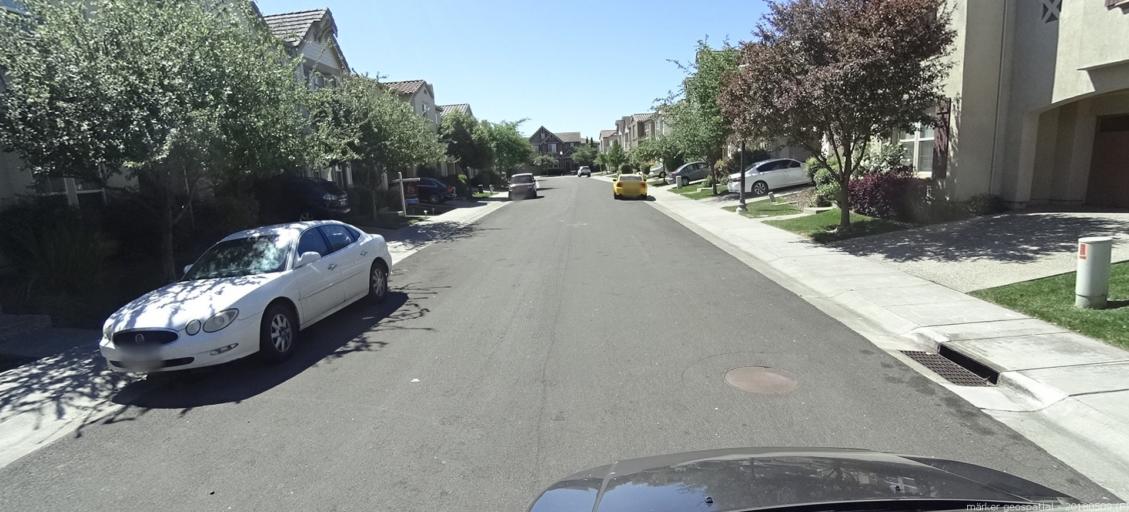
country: US
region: California
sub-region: Sacramento County
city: Elverta
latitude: 38.6735
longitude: -121.5251
